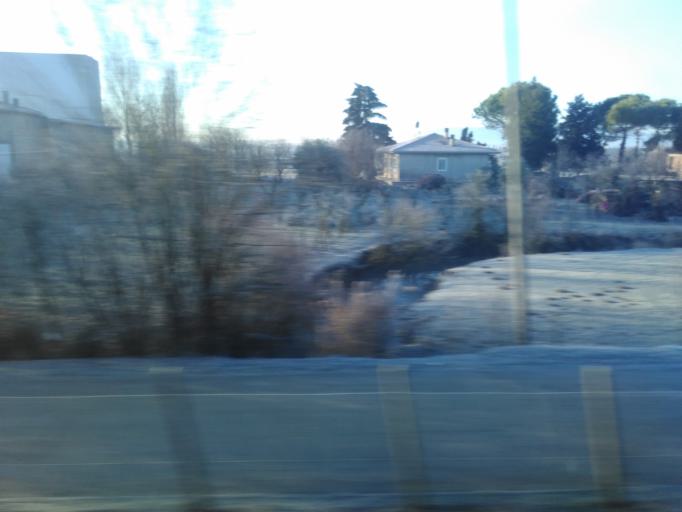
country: IT
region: Veneto
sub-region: Provincia di Vicenza
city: Grumolo delle Abbadesse
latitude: 45.5106
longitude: 11.6543
